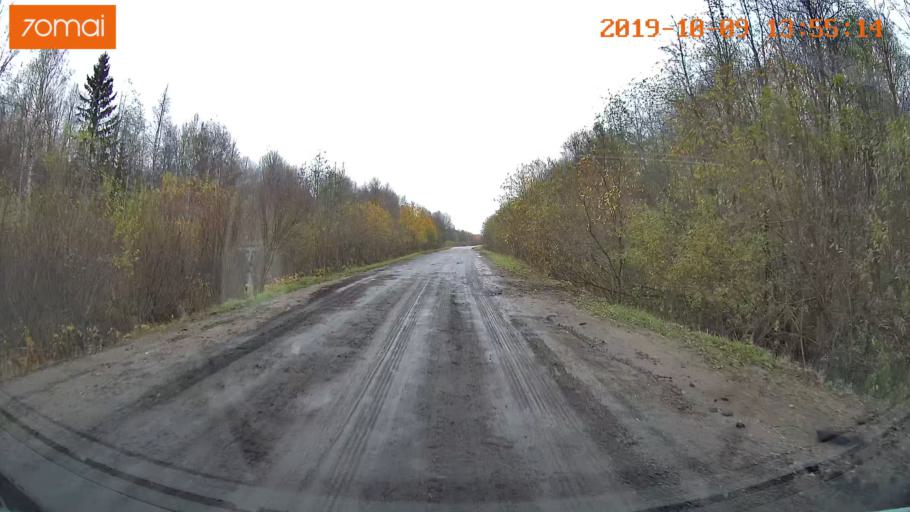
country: RU
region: Kostroma
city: Buy
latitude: 58.4235
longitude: 41.2717
